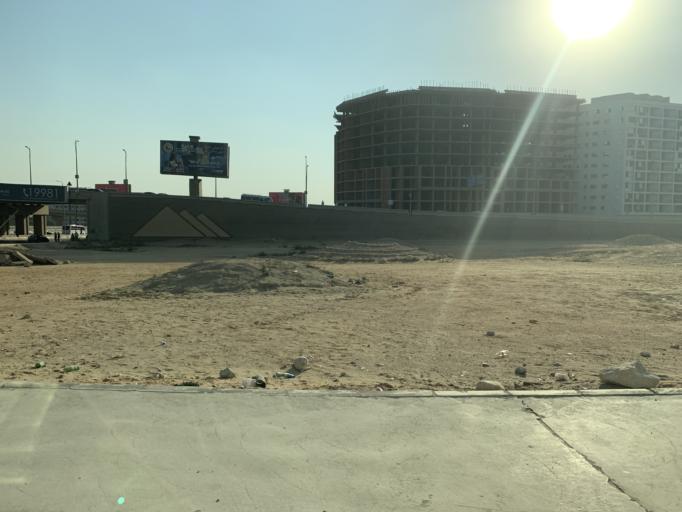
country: EG
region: Al Jizah
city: Al Hawamidiyah
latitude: 29.9796
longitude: 31.3605
